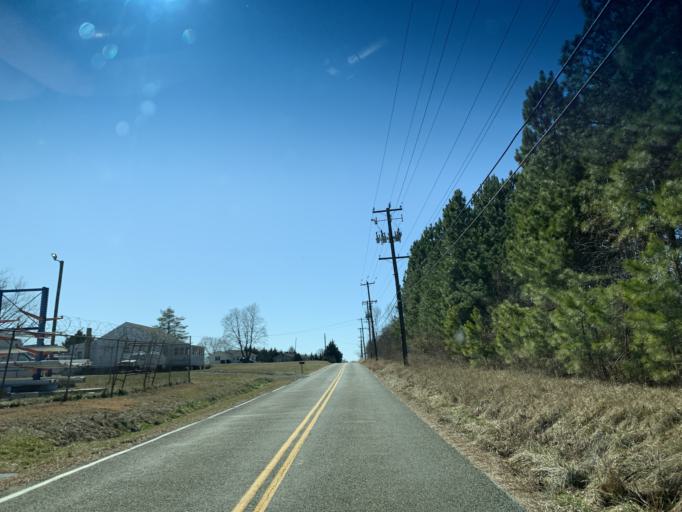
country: US
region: Maryland
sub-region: Cecil County
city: Elkton
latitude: 39.5147
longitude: -75.8263
